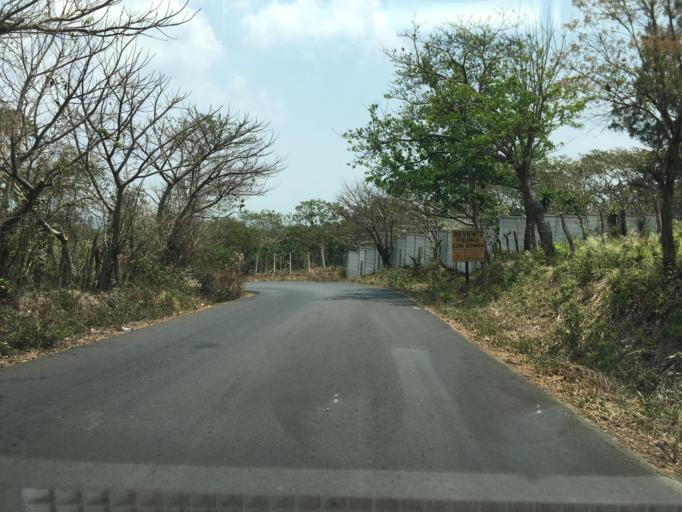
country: GT
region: Santa Rosa
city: Pueblo Nuevo Vinas
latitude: 14.3145
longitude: -90.5443
